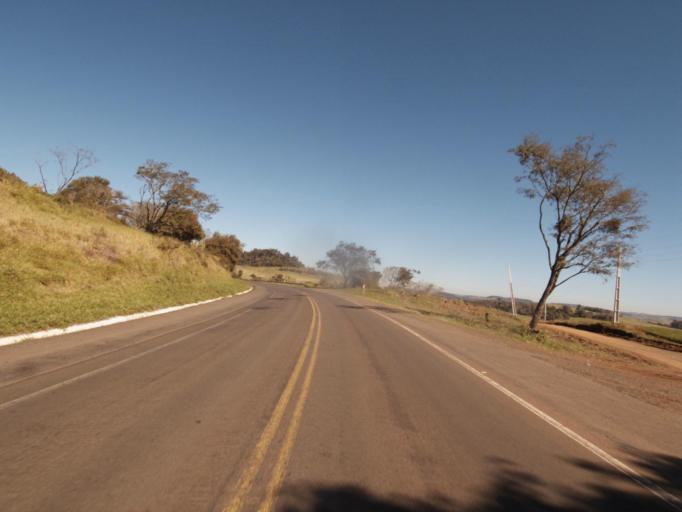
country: BR
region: Rio Grande do Sul
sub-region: Frederico Westphalen
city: Frederico Westphalen
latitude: -26.8048
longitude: -53.3628
